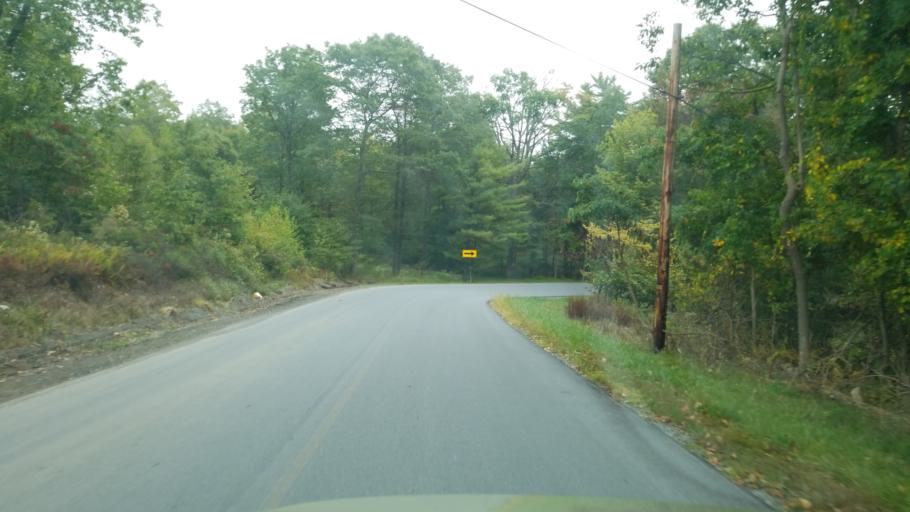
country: US
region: Pennsylvania
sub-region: Clearfield County
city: Curwensville
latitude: 41.0281
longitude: -78.5563
